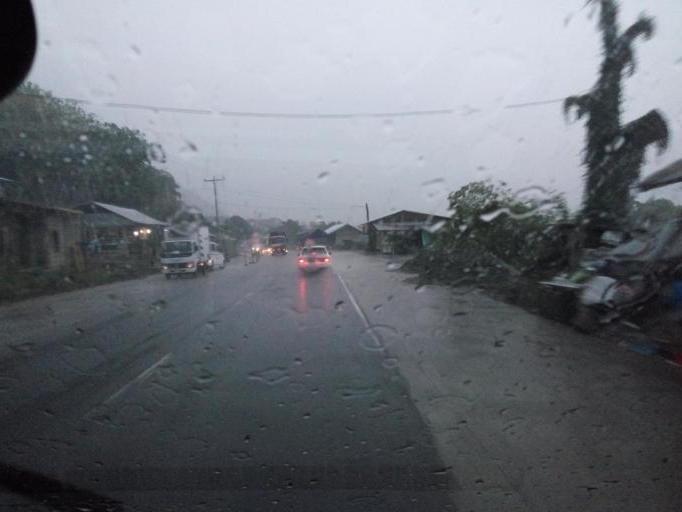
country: PH
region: Cagayan Valley
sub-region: Province of Nueva Vizcaya
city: Bone South
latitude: 16.2241
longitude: 120.9696
